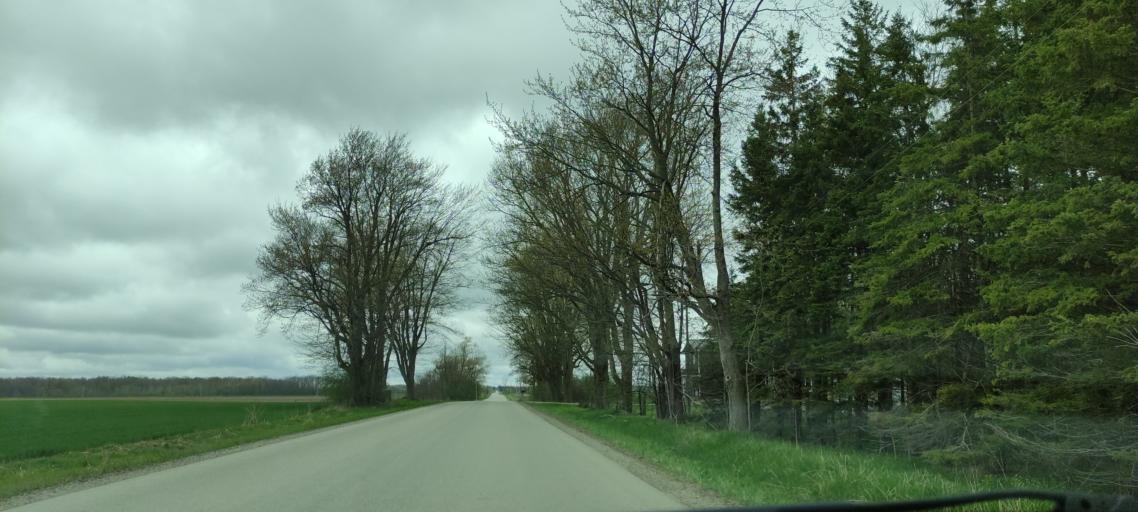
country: CA
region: Ontario
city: Stratford
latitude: 43.4262
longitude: -80.9587
